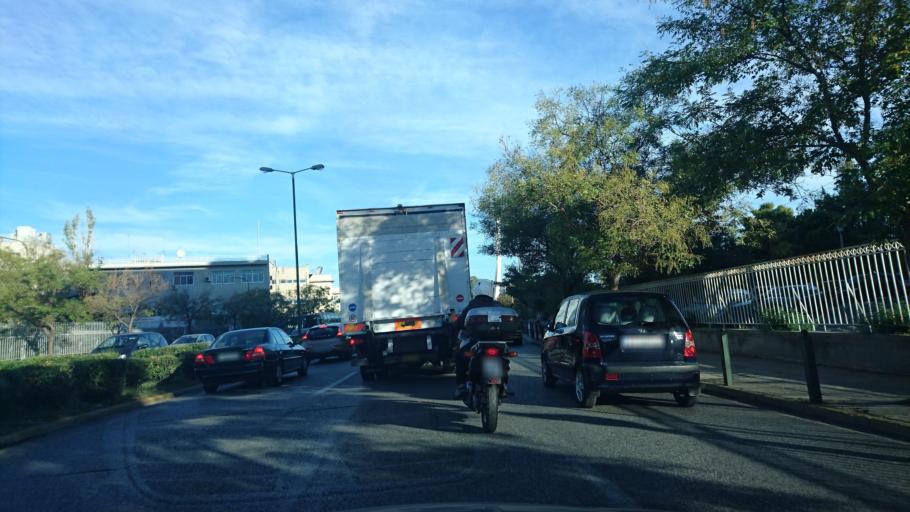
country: GR
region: Attica
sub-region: Nomarchia Athinas
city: Neo Psychiko
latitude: 37.9909
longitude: 23.7773
